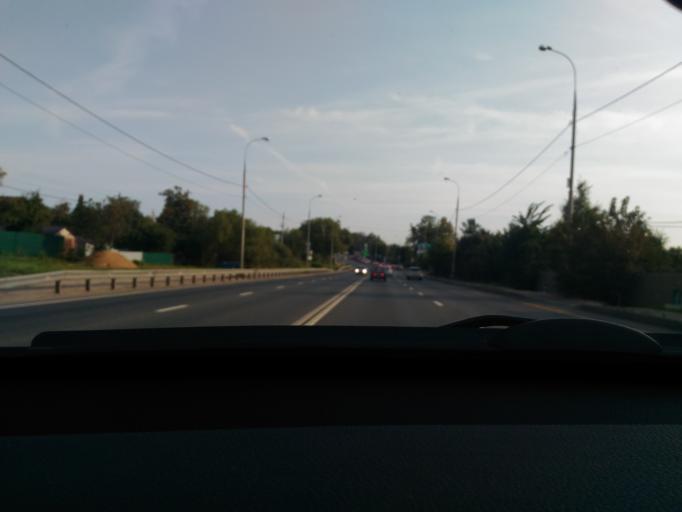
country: RU
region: Moskovskaya
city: Sheremet'yevskiy
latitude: 56.0079
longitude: 37.5437
